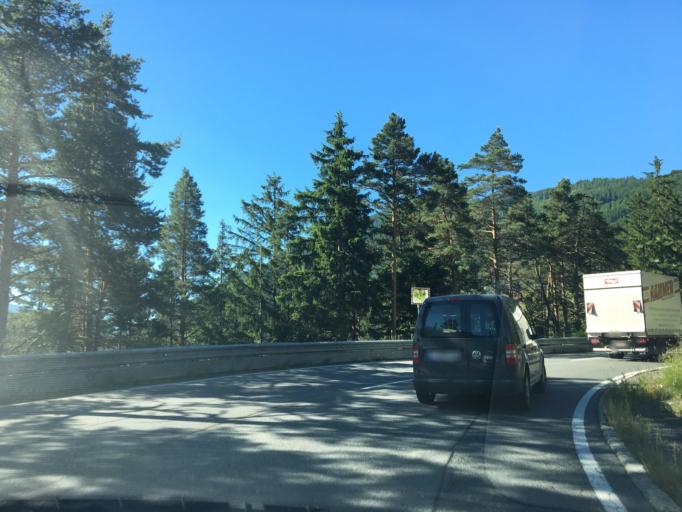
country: AT
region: Tyrol
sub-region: Politischer Bezirk Innsbruck Land
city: Schoenberg im Stubaital
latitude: 47.1889
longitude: 11.4163
